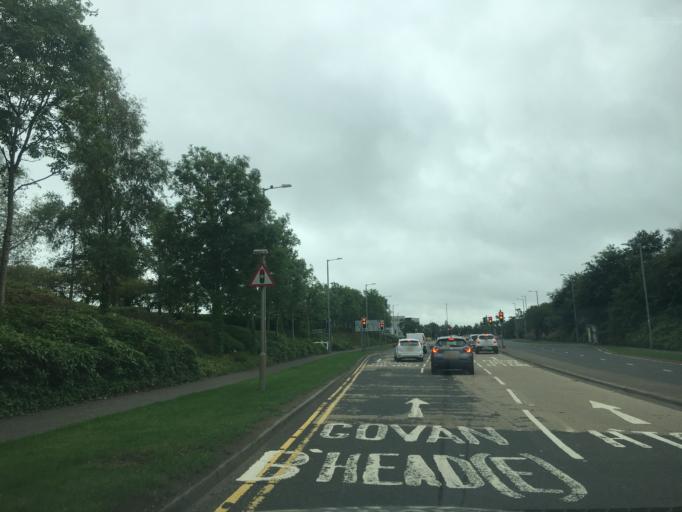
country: GB
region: Scotland
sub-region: Renfrewshire
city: Renfrew
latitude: 55.8753
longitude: -4.3683
